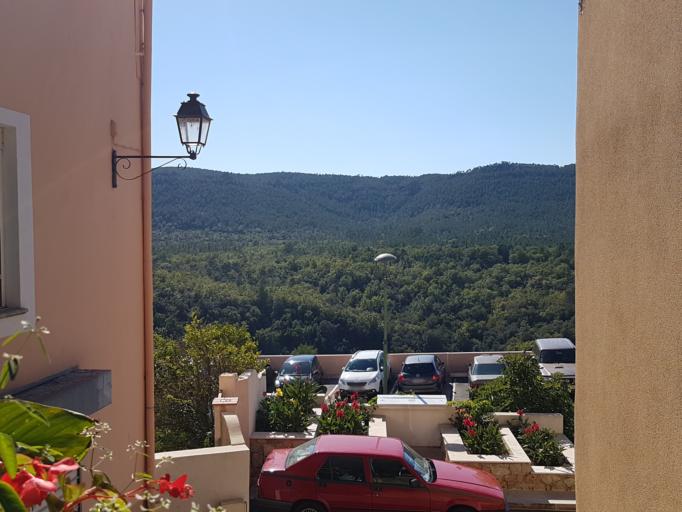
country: FR
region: Provence-Alpes-Cote d'Azur
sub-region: Departement du Var
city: Bagnols-en-Foret
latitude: 43.5369
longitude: 6.6988
